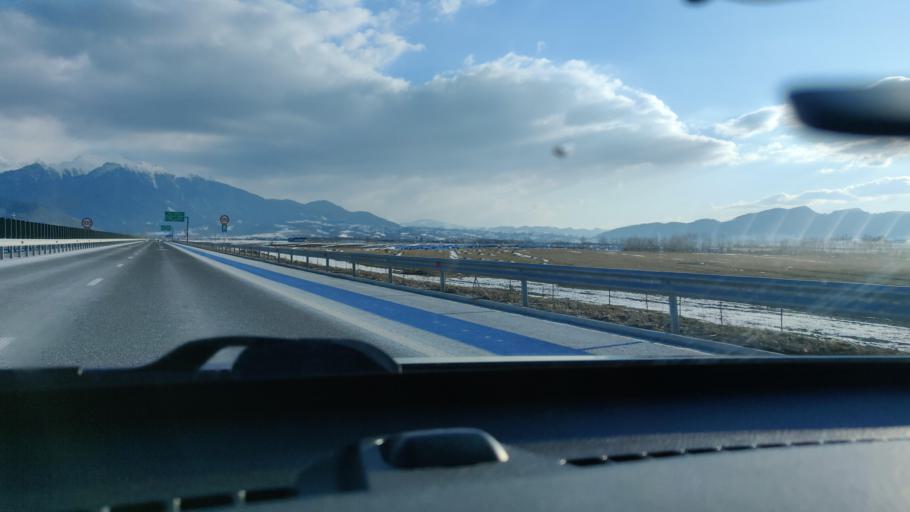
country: RO
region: Brasov
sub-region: Oras Rasnov
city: Rasnov
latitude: 45.5828
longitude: 25.4451
